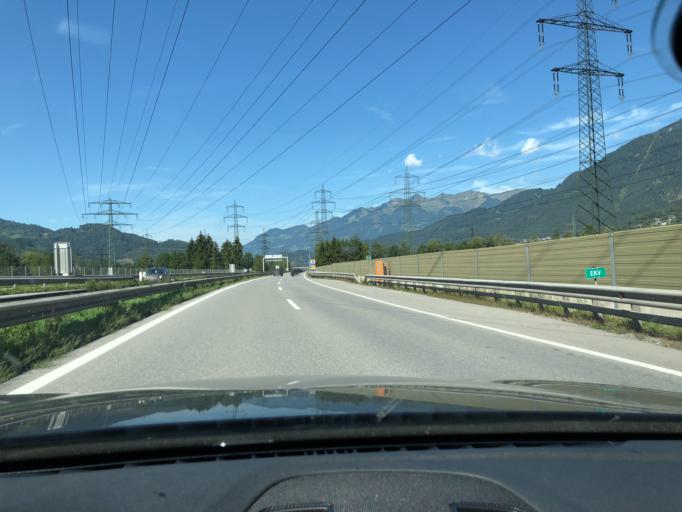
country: AT
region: Vorarlberg
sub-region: Politischer Bezirk Bludenz
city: Bludenz
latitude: 47.1391
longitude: 9.8269
